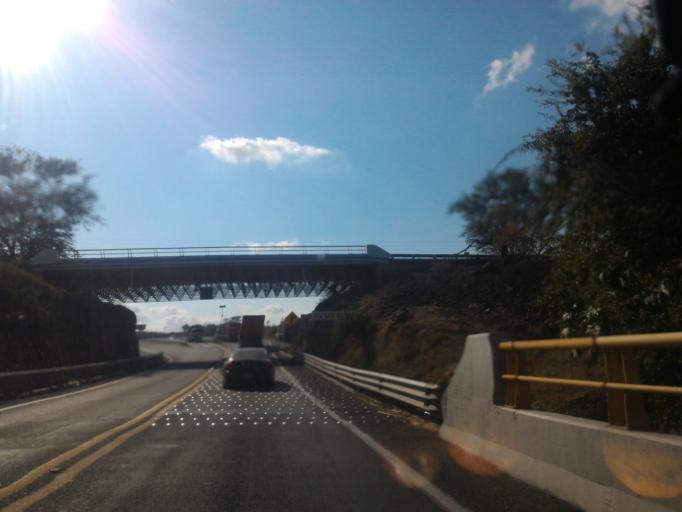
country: MX
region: Jalisco
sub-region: Tonila
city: San Marcos
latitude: 19.4340
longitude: -103.4931
